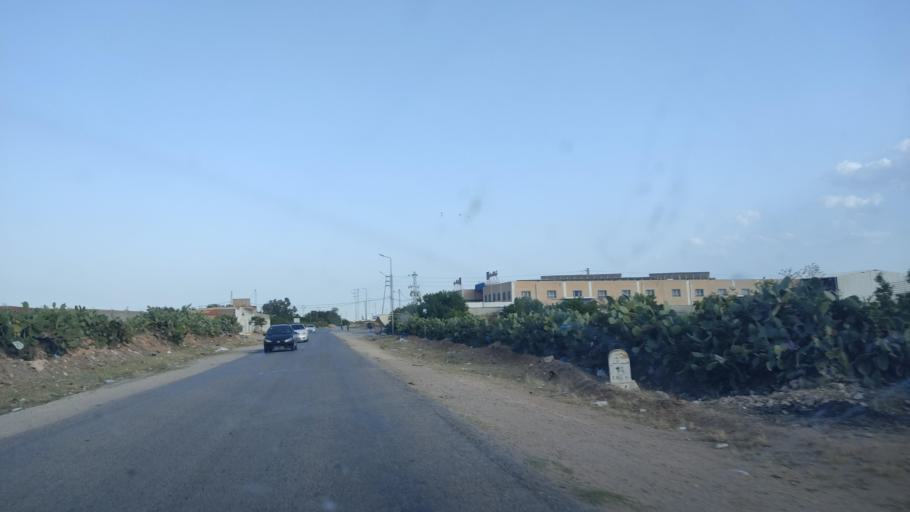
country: TN
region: Safaqis
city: Sfax
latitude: 34.8103
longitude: 10.6630
